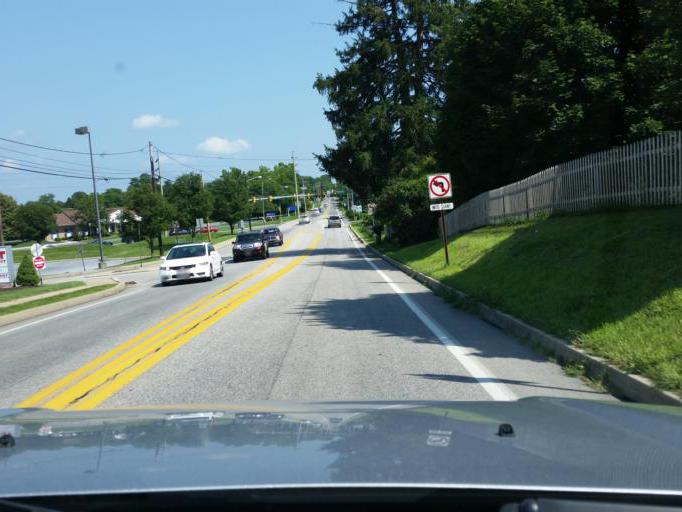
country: US
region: Pennsylvania
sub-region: Dauphin County
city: Hershey
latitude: 40.2683
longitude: -76.6493
